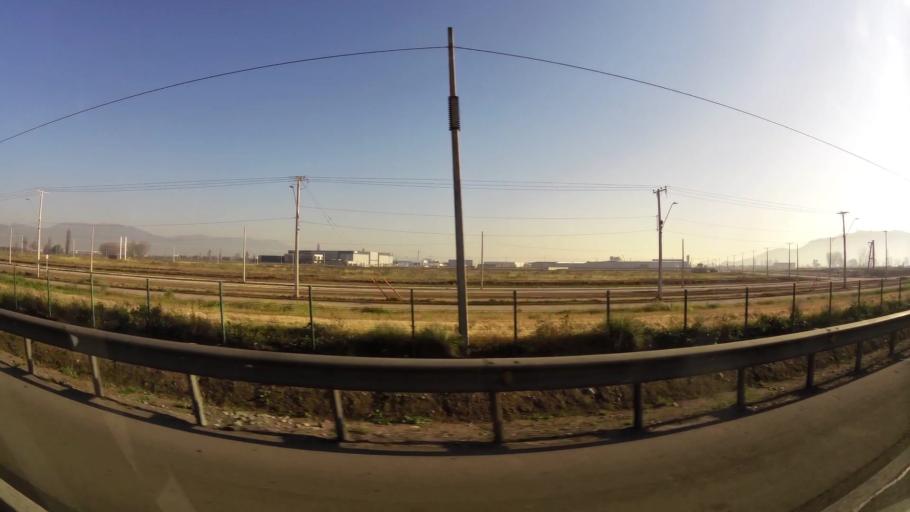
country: CL
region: Santiago Metropolitan
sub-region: Provincia de Santiago
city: Lo Prado
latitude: -33.4126
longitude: -70.7634
